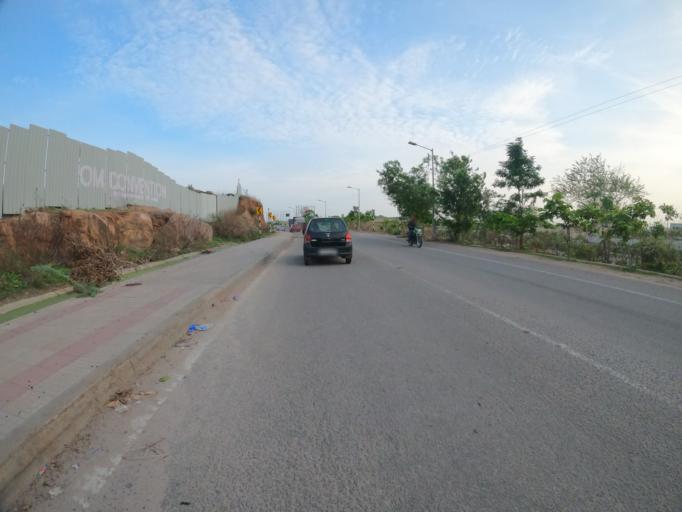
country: IN
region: Telangana
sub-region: Hyderabad
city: Hyderabad
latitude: 17.3874
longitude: 78.3522
